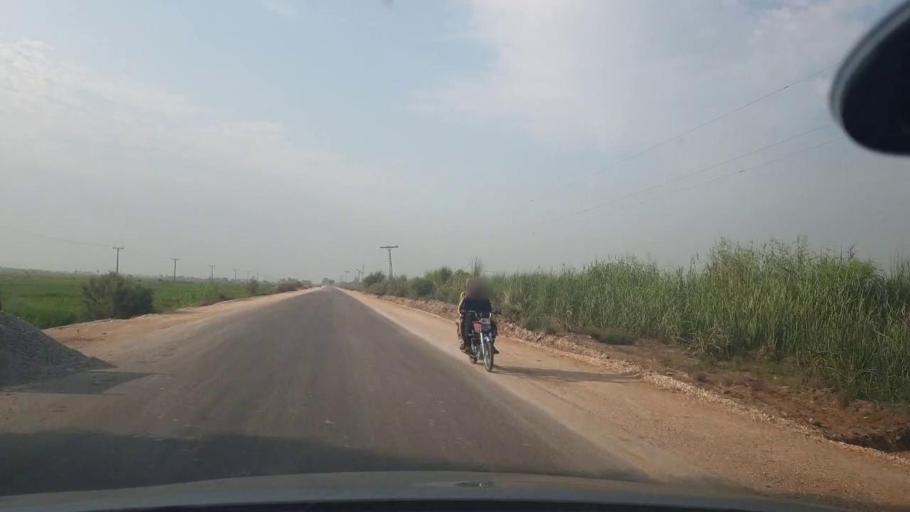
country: PK
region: Sindh
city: Jacobabad
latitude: 28.1830
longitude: 68.3675
